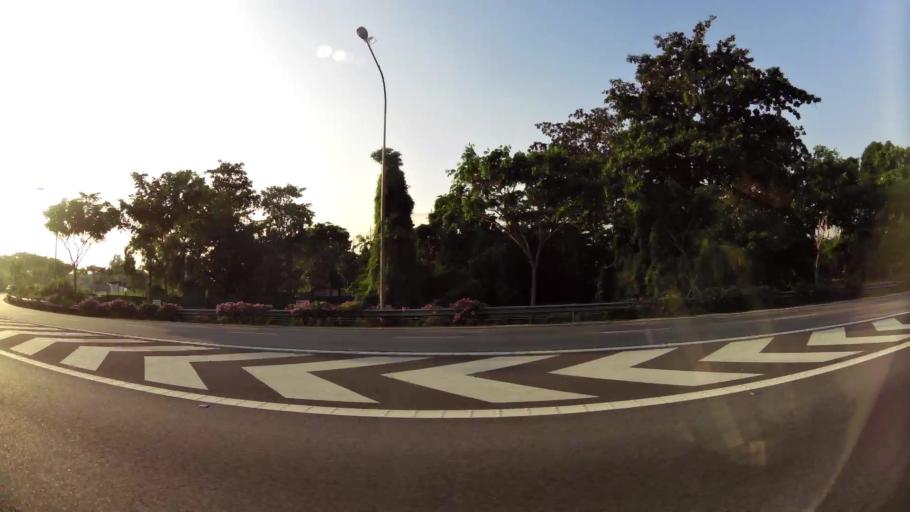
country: SG
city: Singapore
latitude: 1.2952
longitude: 103.8730
